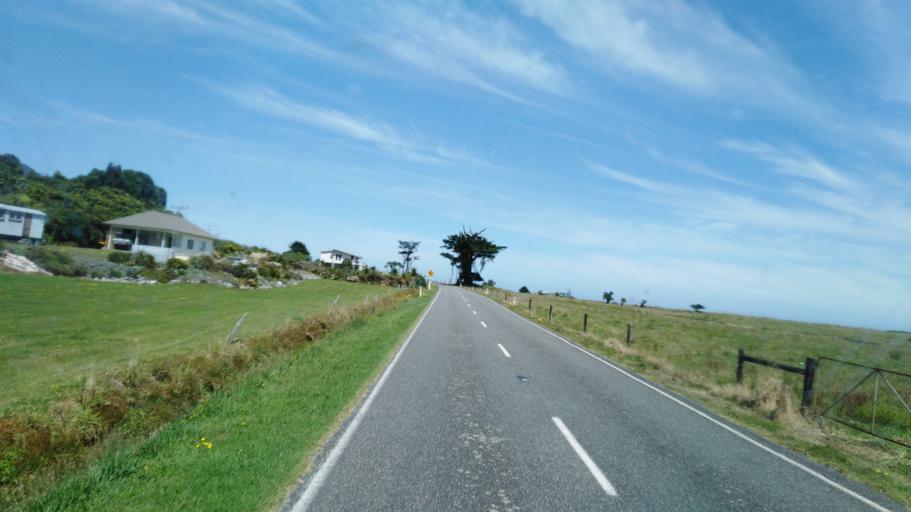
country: NZ
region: West Coast
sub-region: Buller District
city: Westport
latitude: -41.5360
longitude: 171.9324
